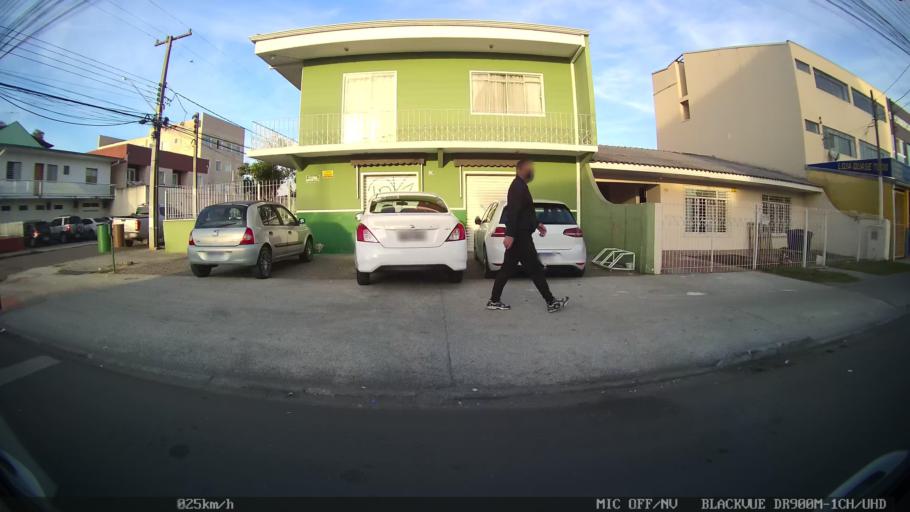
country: BR
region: Parana
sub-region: Pinhais
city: Pinhais
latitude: -25.4421
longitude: -49.1616
